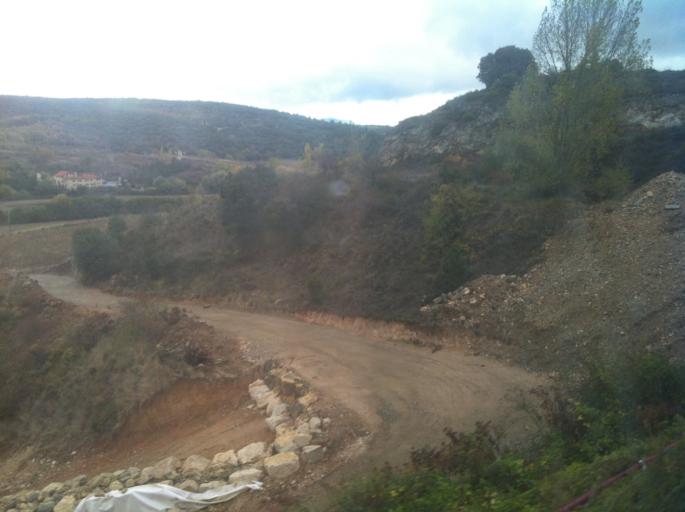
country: ES
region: Castille and Leon
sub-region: Provincia de Burgos
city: Ameyugo
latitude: 42.6473
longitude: -3.0824
